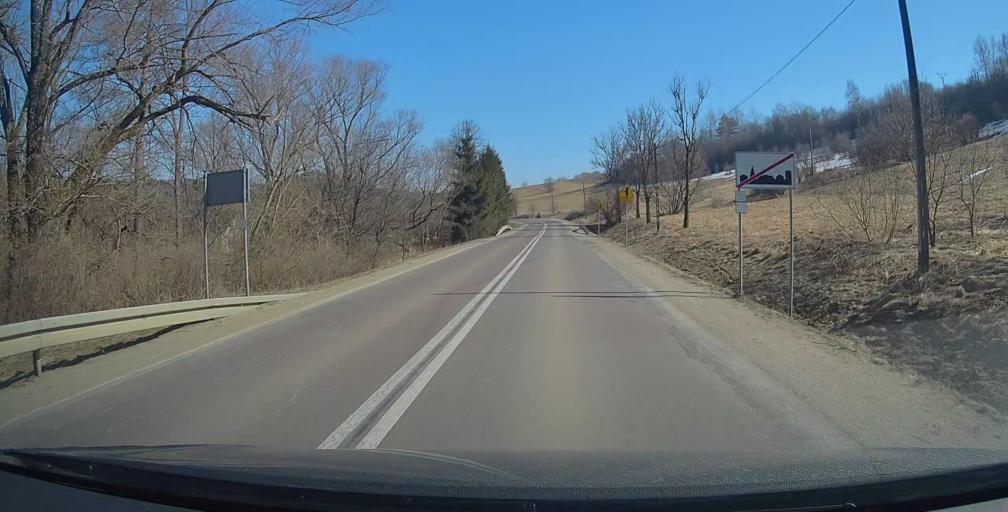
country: PL
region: Subcarpathian Voivodeship
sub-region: Powiat bieszczadzki
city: Ustrzyki Dolne
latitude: 49.5548
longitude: 22.5627
